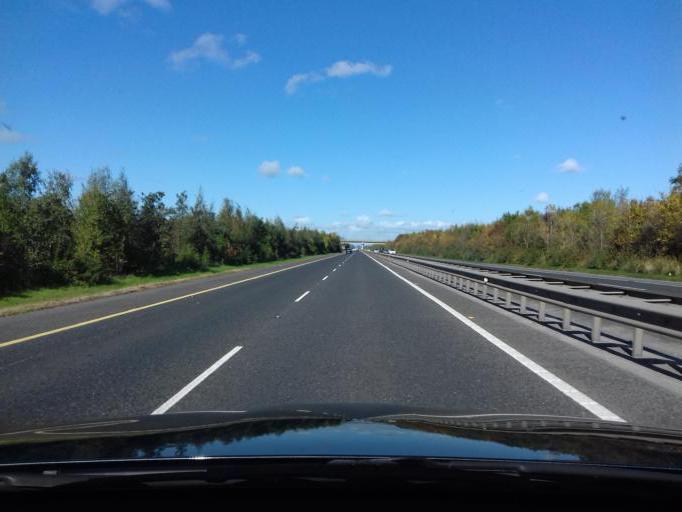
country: IE
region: Leinster
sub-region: An Mhi
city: Ashbourne
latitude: 53.4638
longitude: -6.3581
